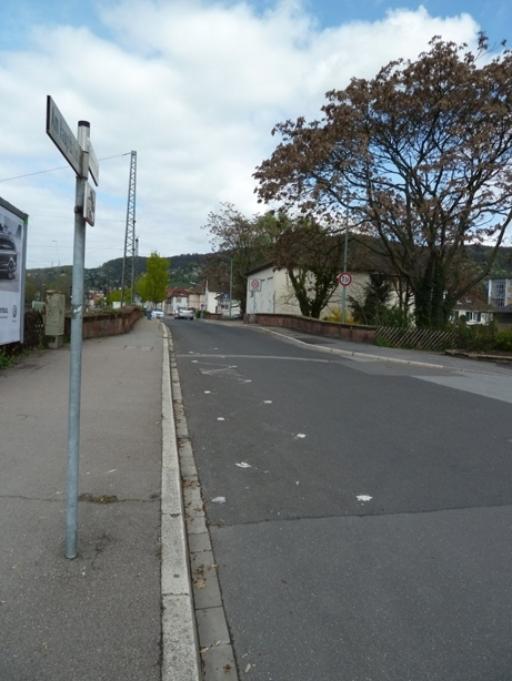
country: DE
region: Baden-Wuerttemberg
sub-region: Karlsruhe Region
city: Weinheim
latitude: 49.5545
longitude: 8.6664
